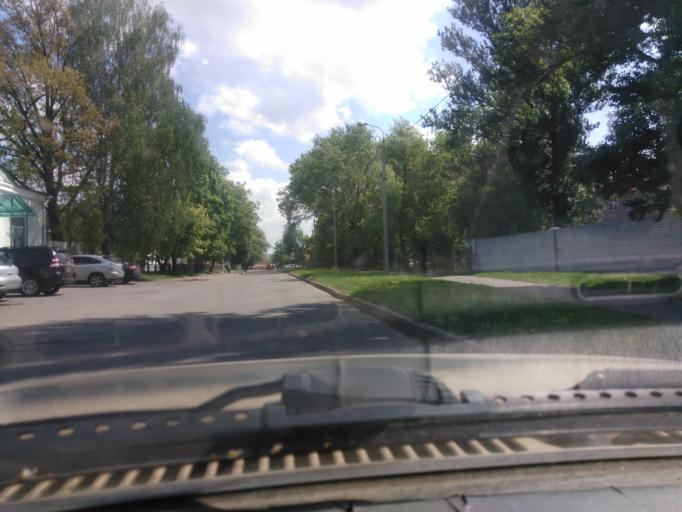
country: BY
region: Mogilev
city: Mahilyow
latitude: 53.9287
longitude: 30.3143
